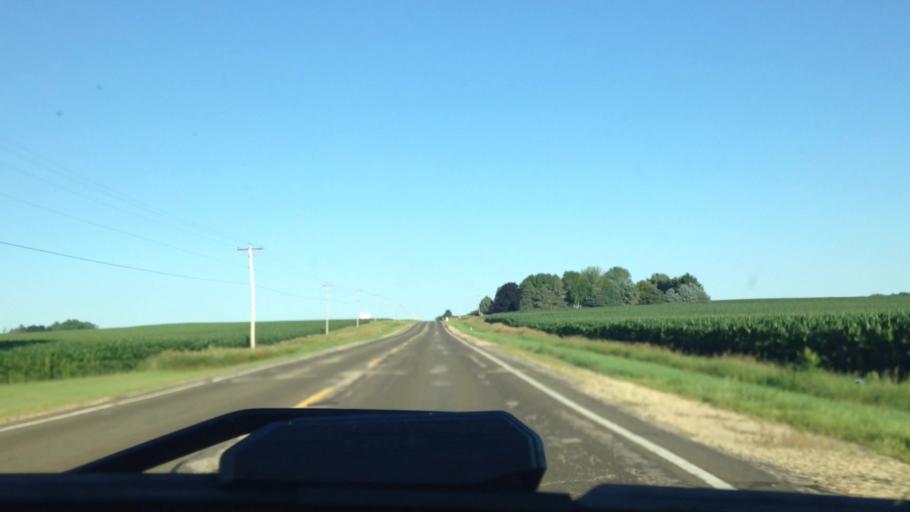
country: US
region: Wisconsin
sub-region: Columbia County
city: Poynette
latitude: 43.3375
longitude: -89.4098
